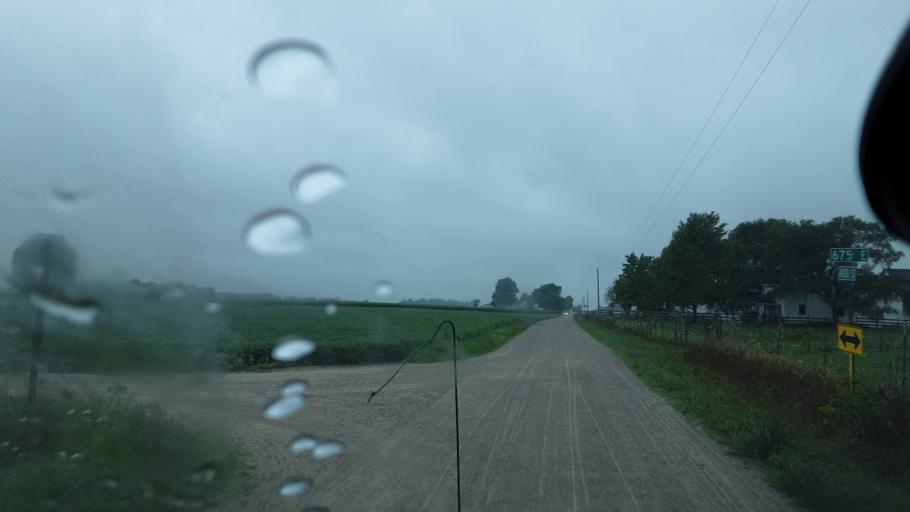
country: US
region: Indiana
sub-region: Adams County
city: Berne
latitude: 40.6894
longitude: -84.8066
